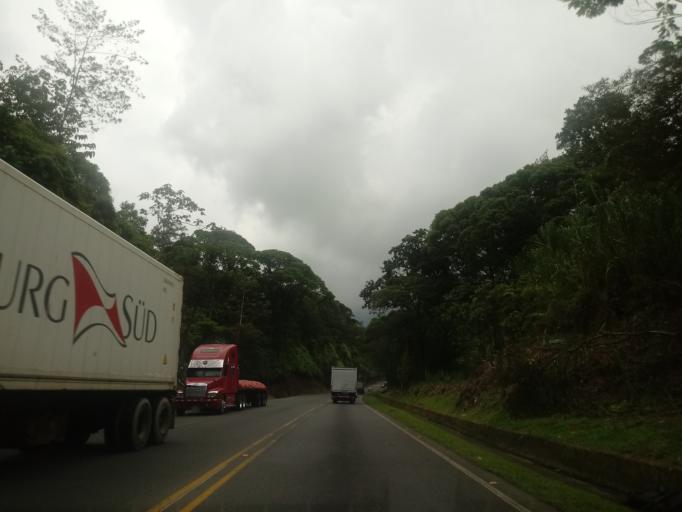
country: CR
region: San Jose
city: Dulce Nombre de Jesus
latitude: 10.1750
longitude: -83.9304
